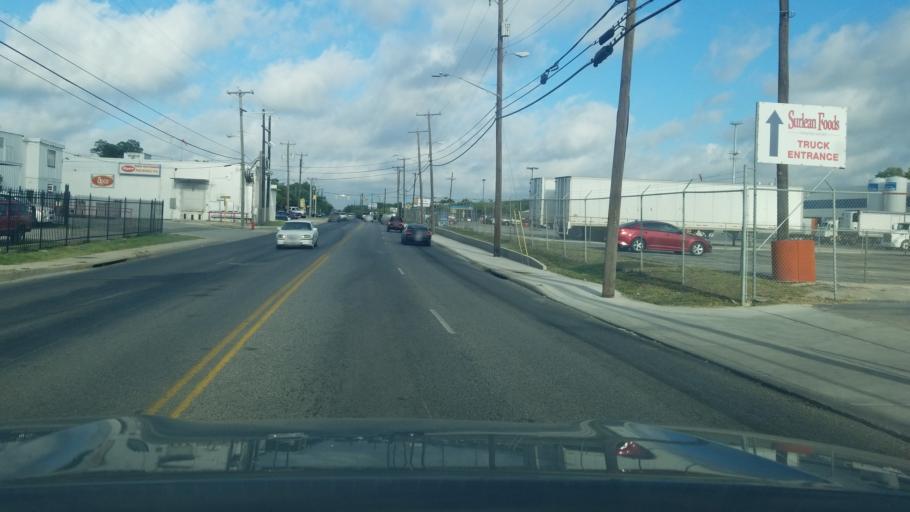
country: US
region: Texas
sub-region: Bexar County
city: San Antonio
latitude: 29.4119
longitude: -98.5133
